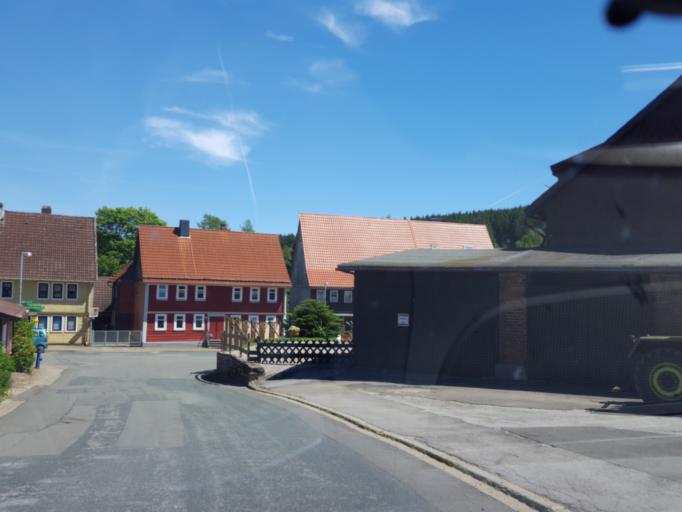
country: DE
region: Lower Saxony
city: Clausthal-Zellerfeld
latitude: 51.7773
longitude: 10.3317
